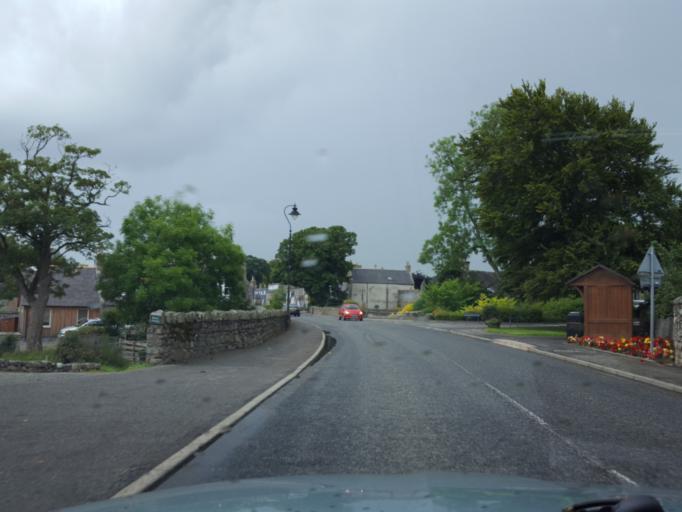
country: GB
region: Scotland
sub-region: Aberdeenshire
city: Torphins
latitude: 57.0855
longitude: -2.6728
